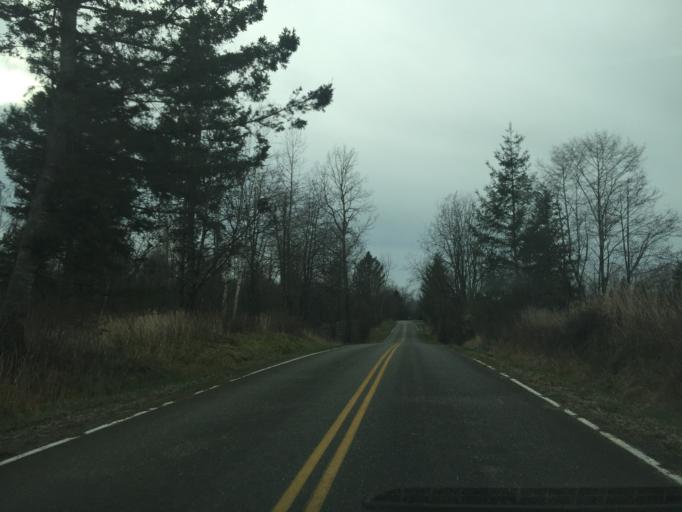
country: US
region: Washington
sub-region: Whatcom County
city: Everson
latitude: 48.9494
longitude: -122.3719
